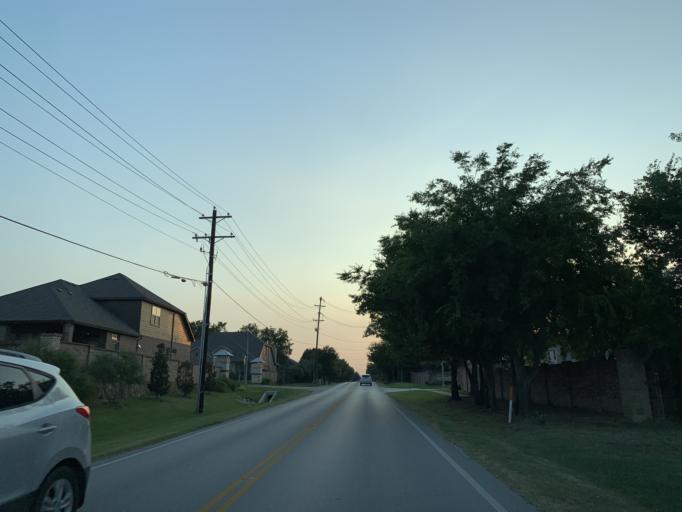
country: US
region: Texas
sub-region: Tarrant County
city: Keller
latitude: 32.9636
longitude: -97.2581
